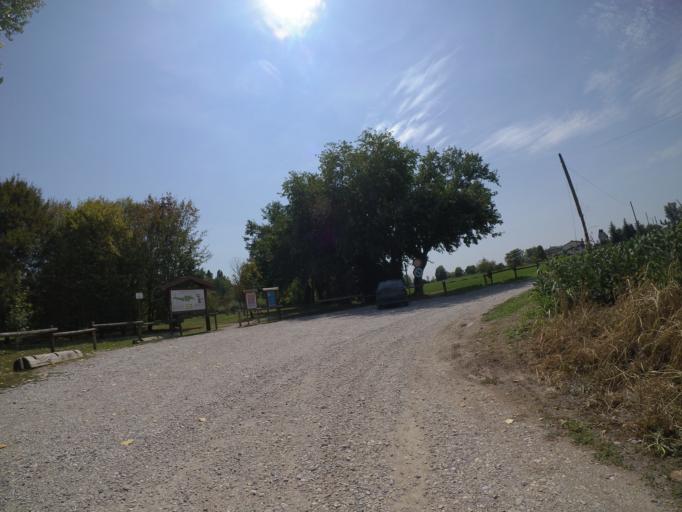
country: IT
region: Friuli Venezia Giulia
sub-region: Provincia di Udine
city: Codroipo
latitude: 45.9546
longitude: 12.9785
